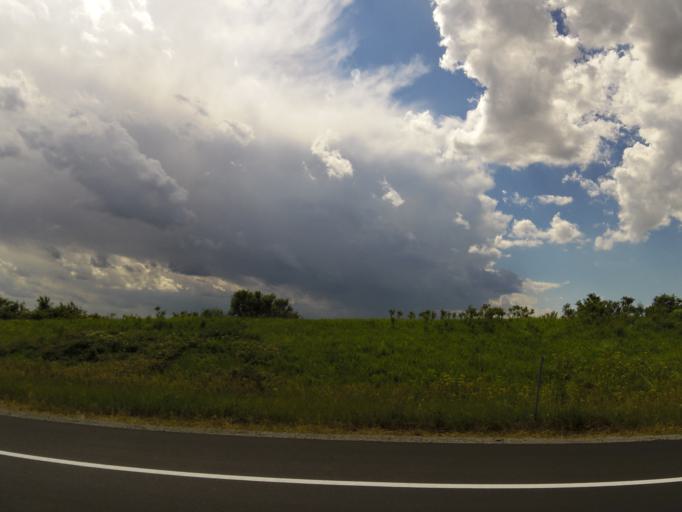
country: US
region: Iowa
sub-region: Johnson County
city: University Heights
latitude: 41.5898
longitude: -91.5459
